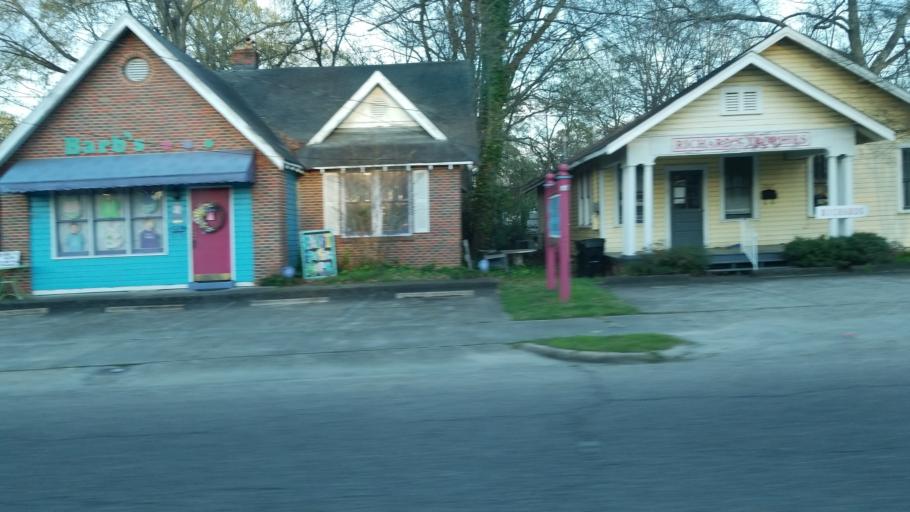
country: US
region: Alabama
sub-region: Montgomery County
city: Montgomery
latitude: 32.3605
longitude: -86.2833
